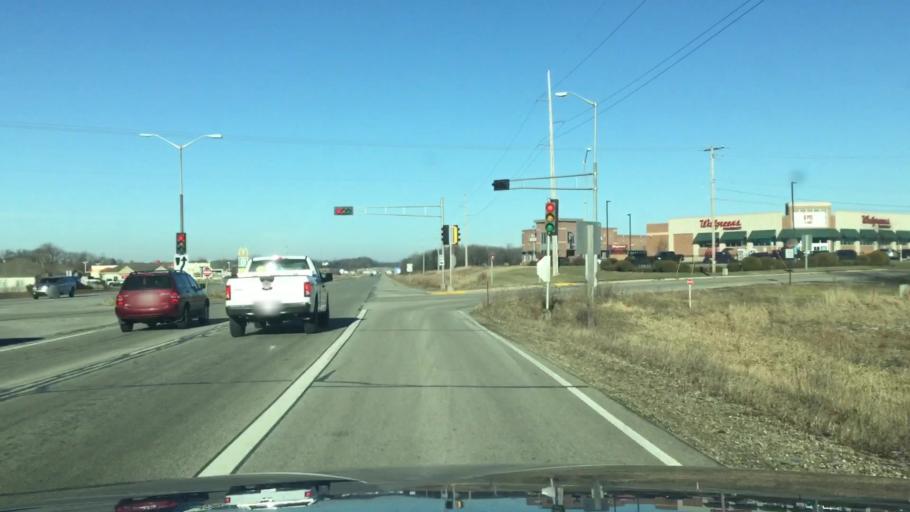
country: US
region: Wisconsin
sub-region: Racine County
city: Waterford
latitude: 42.7627
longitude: -88.1987
